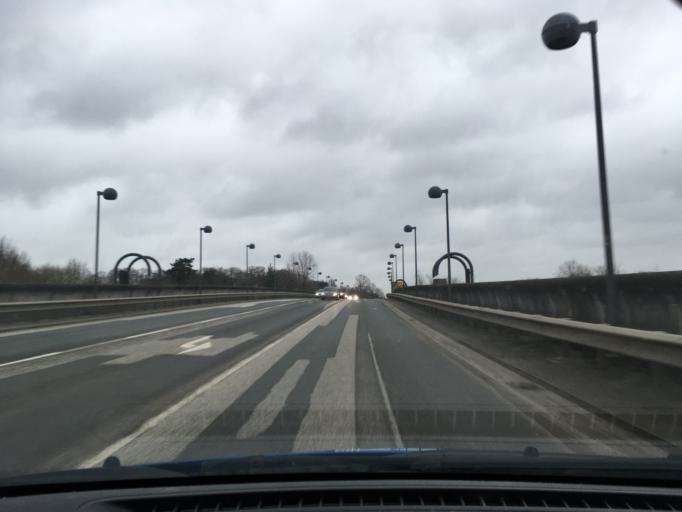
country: DE
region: Schleswig-Holstein
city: Schwarzenbek
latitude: 53.5035
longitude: 10.4762
